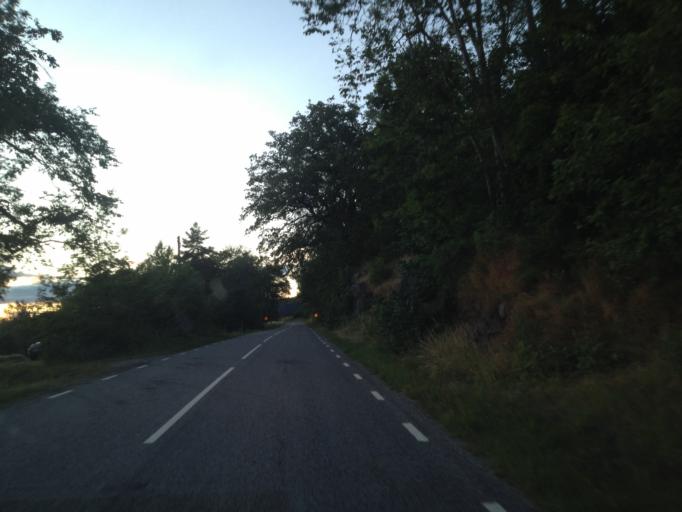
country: SE
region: Kalmar
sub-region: Vasterviks Kommun
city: Overum
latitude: 57.9889
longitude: 16.1874
